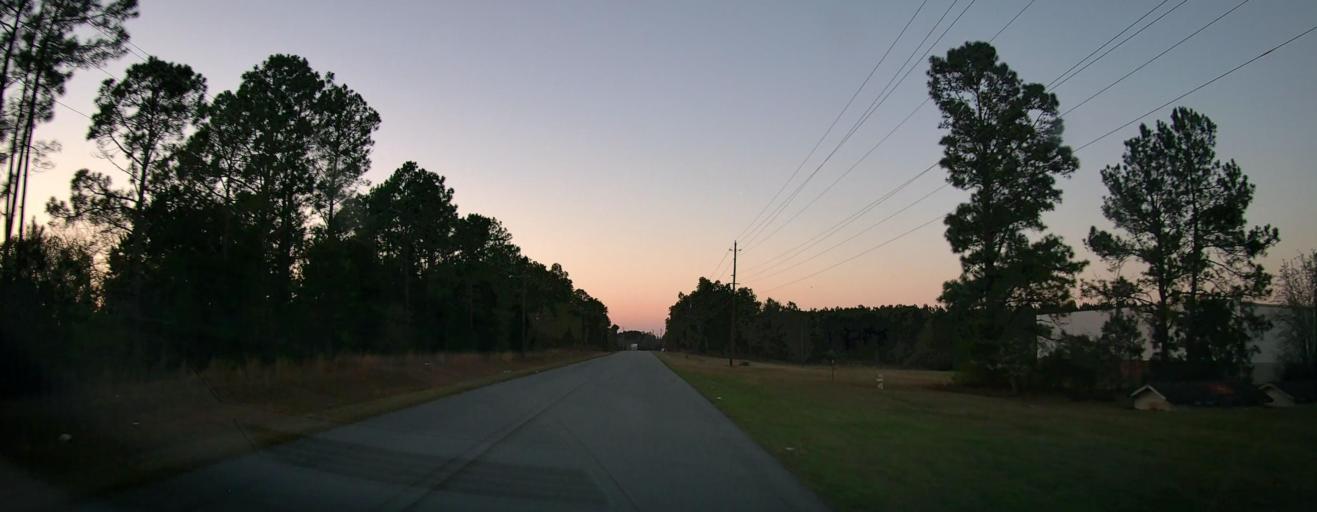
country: US
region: Georgia
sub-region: Dodge County
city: Eastman
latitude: 32.1654
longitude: -83.1518
